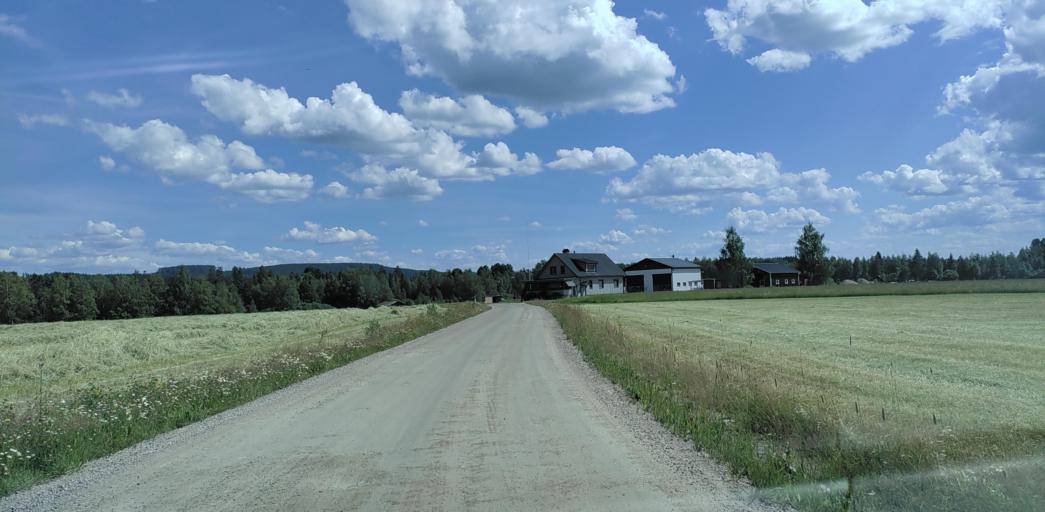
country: SE
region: Vaermland
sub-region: Hagfors Kommun
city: Ekshaerad
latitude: 60.1305
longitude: 13.4649
